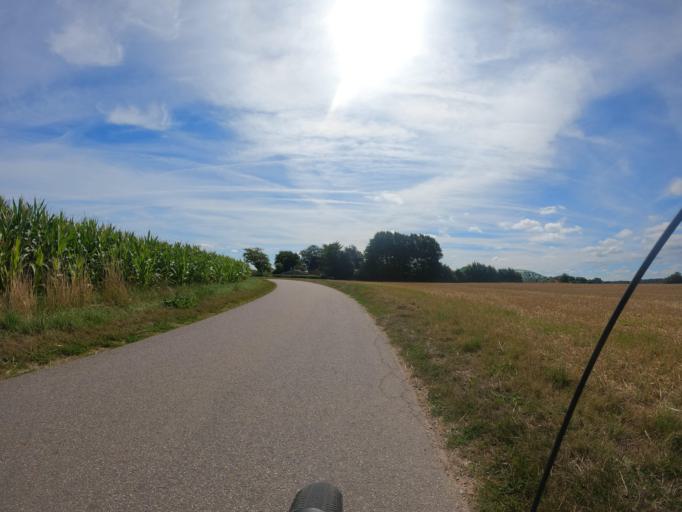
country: DE
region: Schleswig-Holstein
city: Steinbergkirche
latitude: 54.7758
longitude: 9.7603
